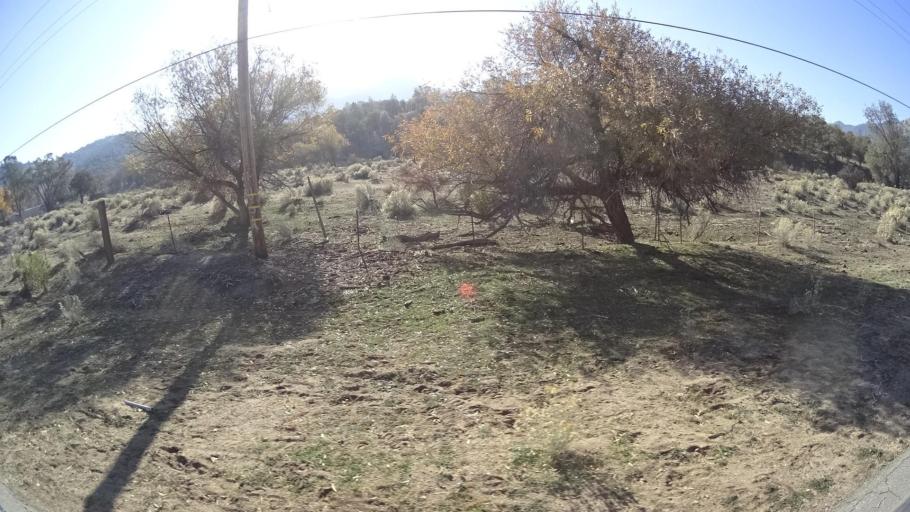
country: US
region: California
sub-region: Kern County
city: Tehachapi
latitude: 35.3113
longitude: -118.4157
